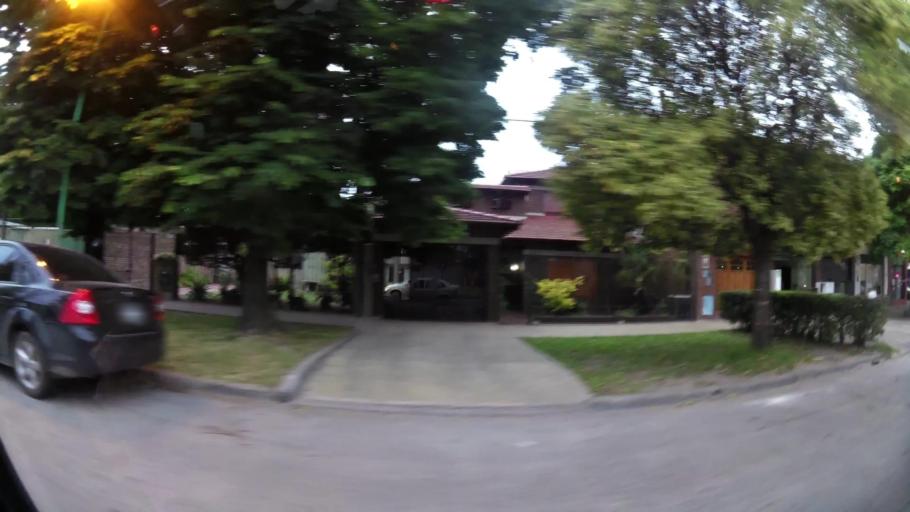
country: AR
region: Buenos Aires
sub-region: Partido de La Plata
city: La Plata
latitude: -34.9135
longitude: -57.9830
